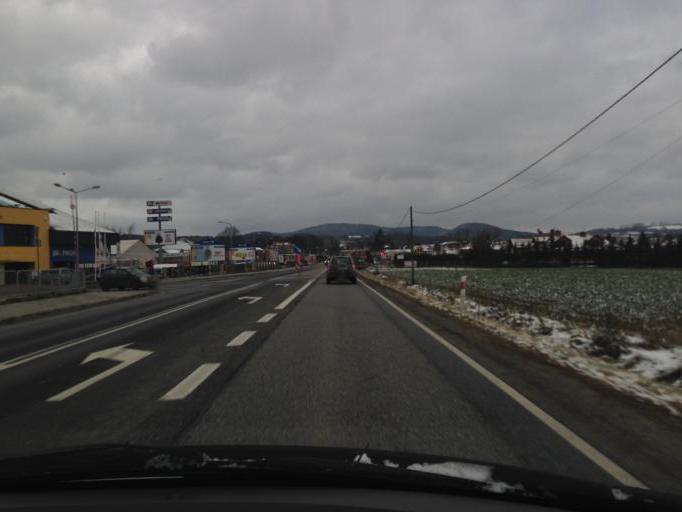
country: PL
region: Lesser Poland Voivodeship
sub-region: Powiat tarnowski
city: Zakliczyn
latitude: 49.8609
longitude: 20.8136
